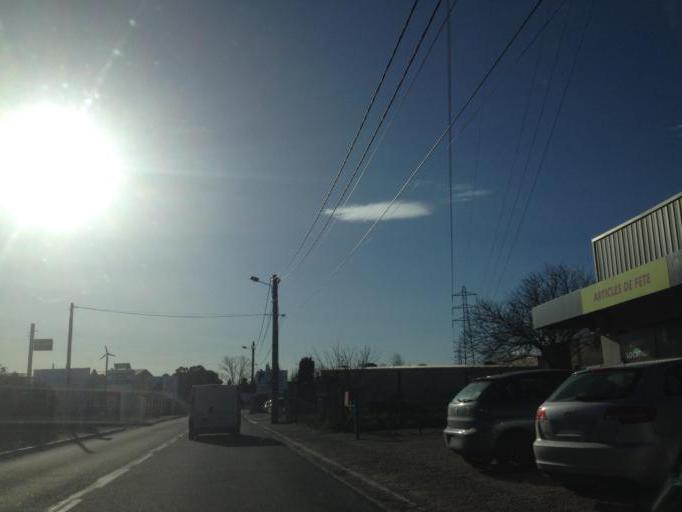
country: FR
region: Provence-Alpes-Cote d'Azur
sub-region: Departement du Vaucluse
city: Orange
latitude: 44.1259
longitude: 4.8392
